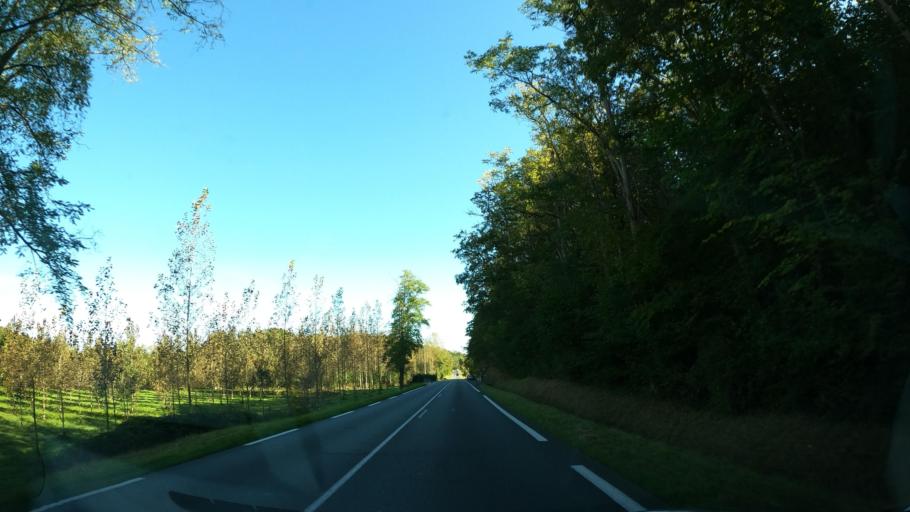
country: FR
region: Aquitaine
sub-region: Departement de la Dordogne
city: Lembras
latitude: 44.9396
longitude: 0.5659
